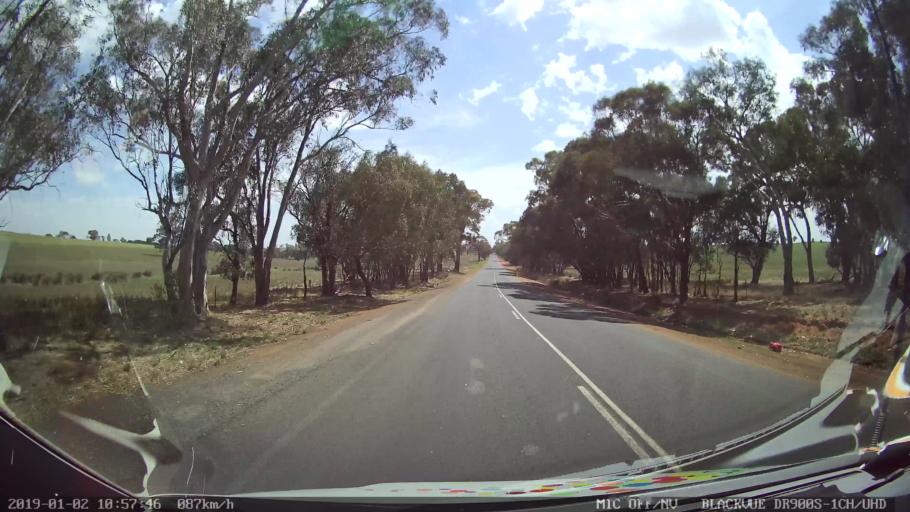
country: AU
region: New South Wales
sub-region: Cootamundra
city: Cootamundra
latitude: -34.6315
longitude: 148.2850
